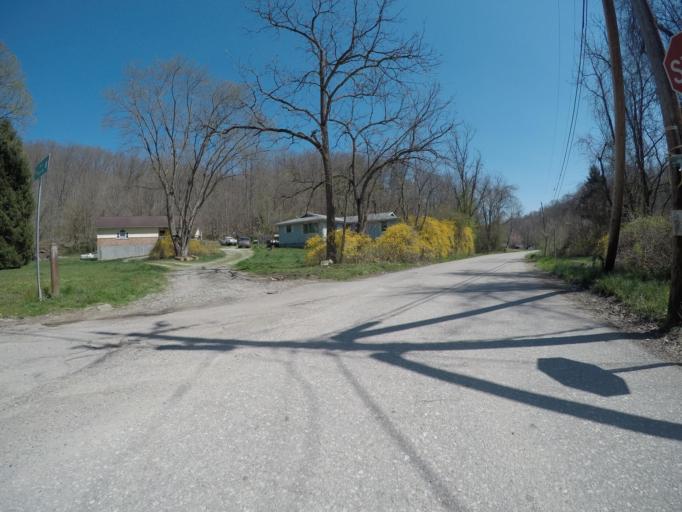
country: US
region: West Virginia
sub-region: Kanawha County
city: Charleston
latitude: 38.4180
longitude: -81.5832
